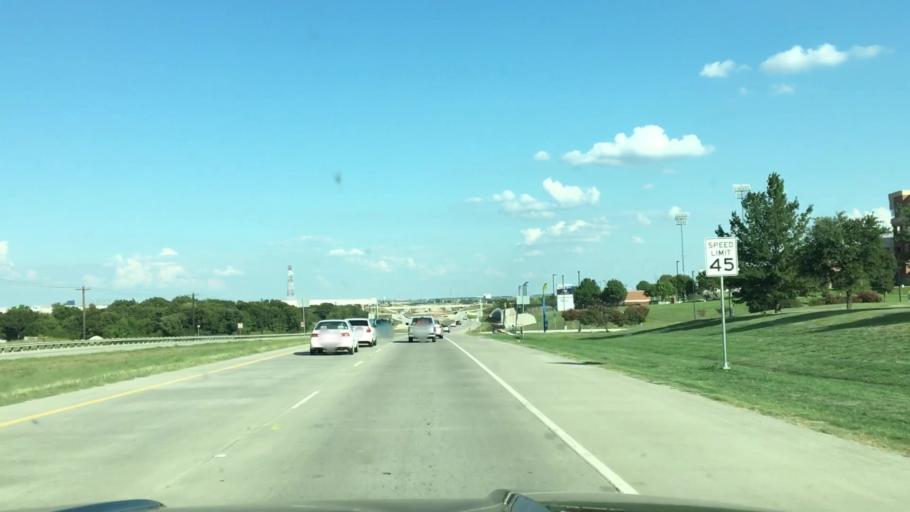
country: US
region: Texas
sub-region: Denton County
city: Justin
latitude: 33.0338
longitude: -97.3218
